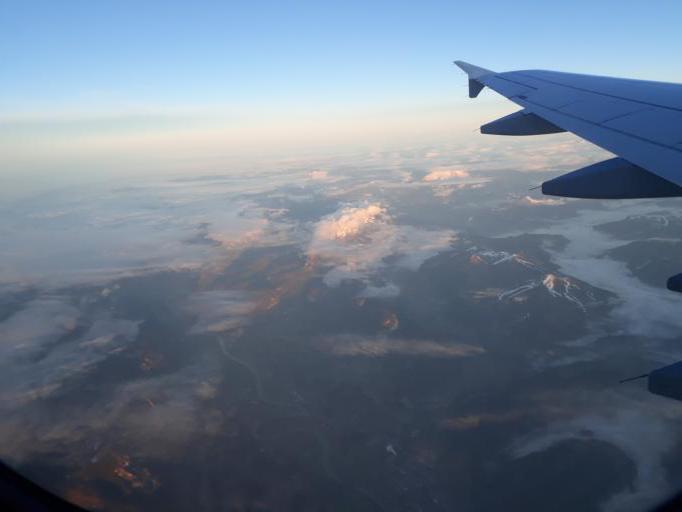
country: AT
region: Tyrol
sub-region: Politischer Bezirk Kufstein
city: Radfeld
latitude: 47.4676
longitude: 11.9403
